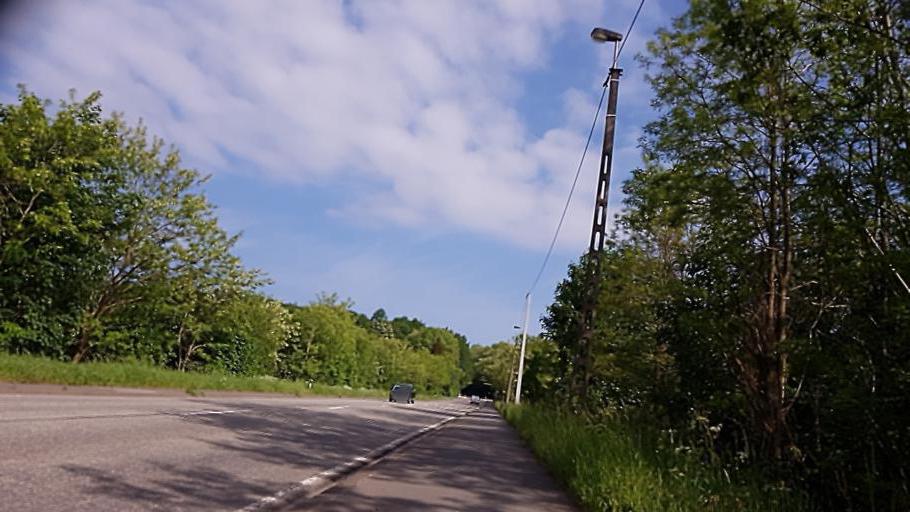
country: BE
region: Flanders
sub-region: Provincie Vlaams-Brabant
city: Huldenberg
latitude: 50.7538
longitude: 4.5711
